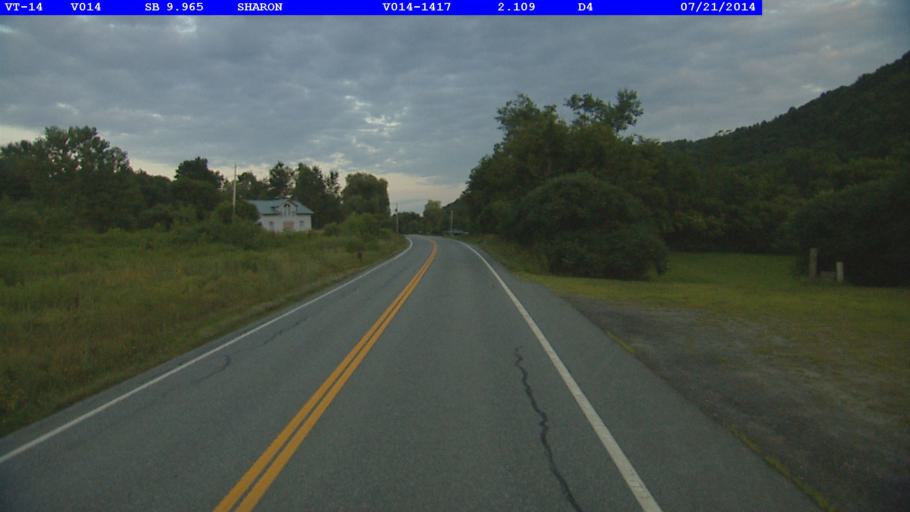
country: US
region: Vermont
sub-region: Windsor County
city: Woodstock
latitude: 43.7477
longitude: -72.4454
